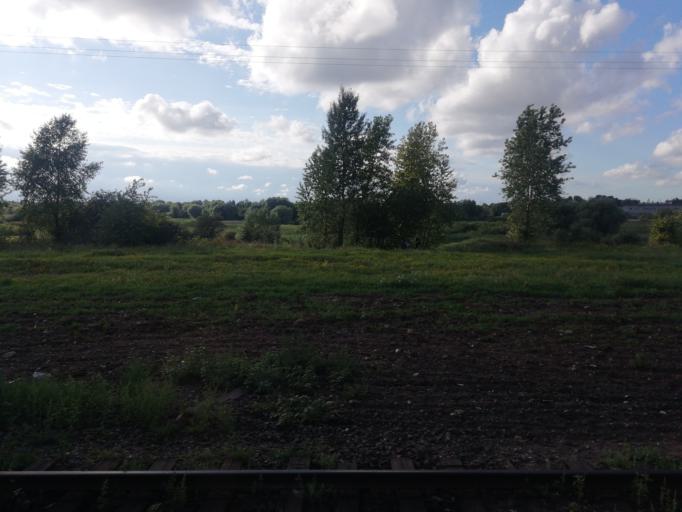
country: RU
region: Kaliningrad
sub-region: Gorod Kaliningrad
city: Kaliningrad
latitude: 54.6853
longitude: 20.4746
